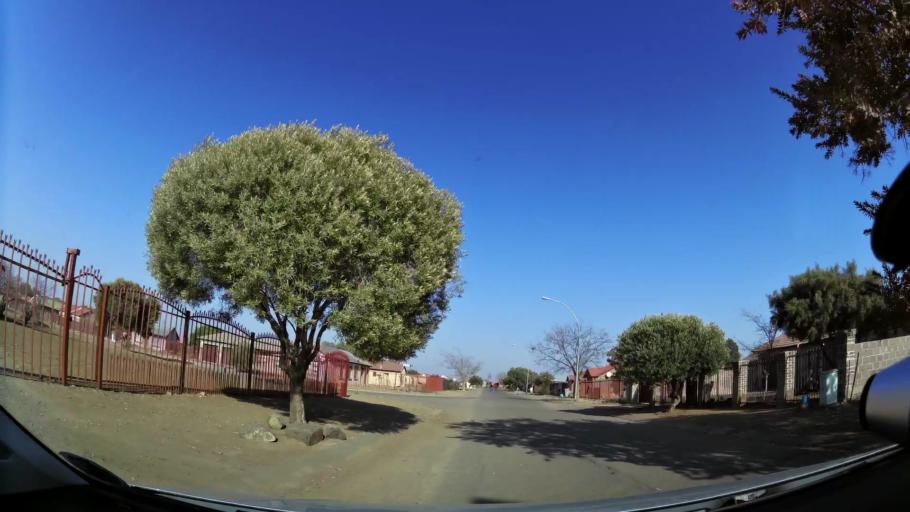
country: ZA
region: Orange Free State
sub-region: Mangaung Metropolitan Municipality
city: Bloemfontein
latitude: -29.1826
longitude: 26.1736
